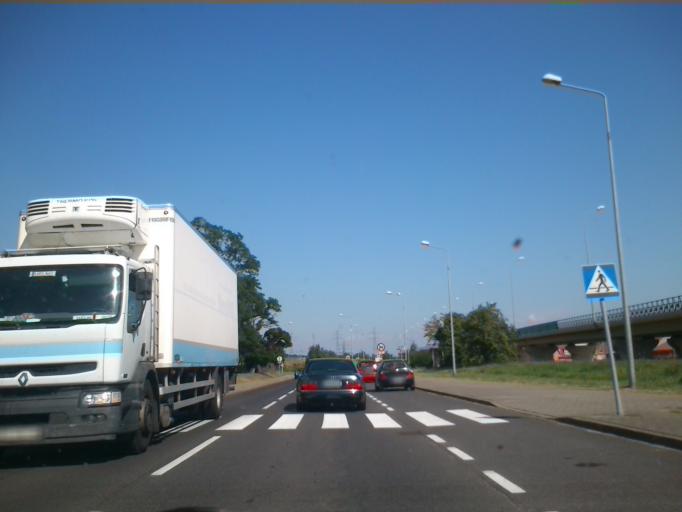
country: PL
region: West Pomeranian Voivodeship
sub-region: Powiat kamienski
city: Wolin
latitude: 53.8483
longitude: 14.6091
